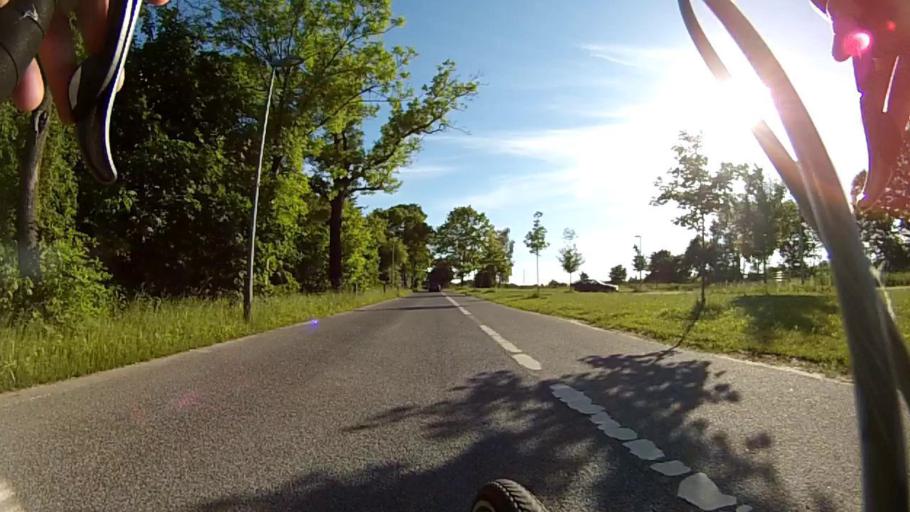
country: DE
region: Brandenburg
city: Ahrensfelde
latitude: 52.6045
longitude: 13.6108
